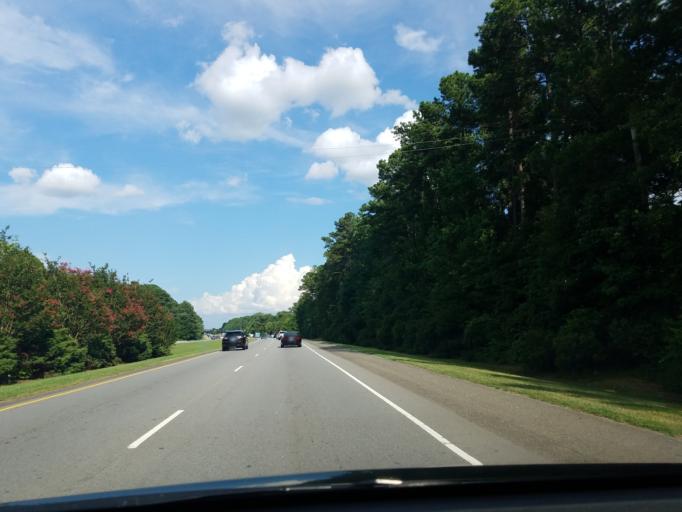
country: US
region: North Carolina
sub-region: Wake County
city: Apex
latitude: 35.7452
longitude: -78.8284
